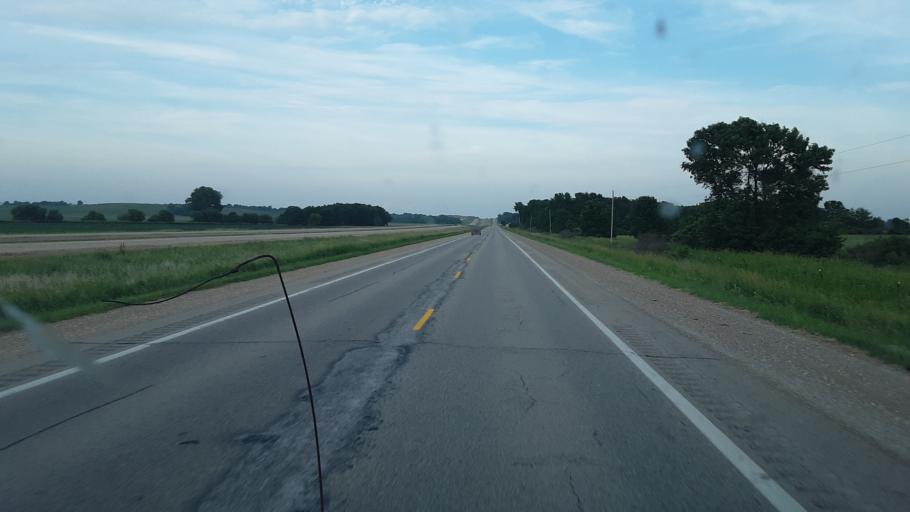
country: US
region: Iowa
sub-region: Tama County
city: Tama
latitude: 41.9638
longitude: -92.4820
